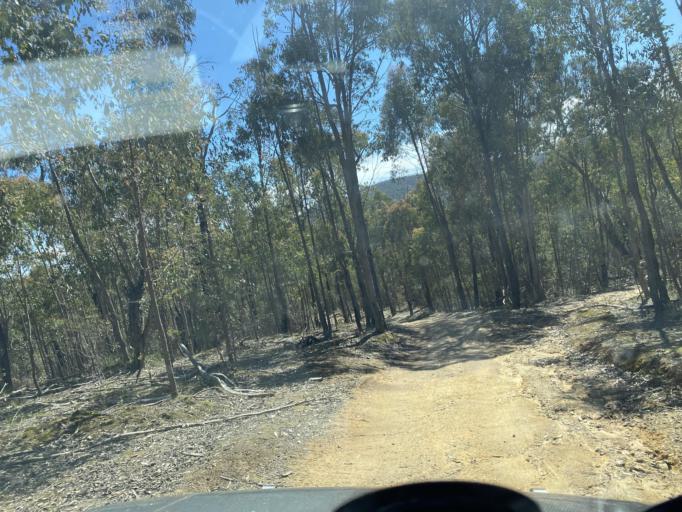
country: AU
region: Victoria
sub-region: Benalla
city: Benalla
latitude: -36.7168
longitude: 146.1810
